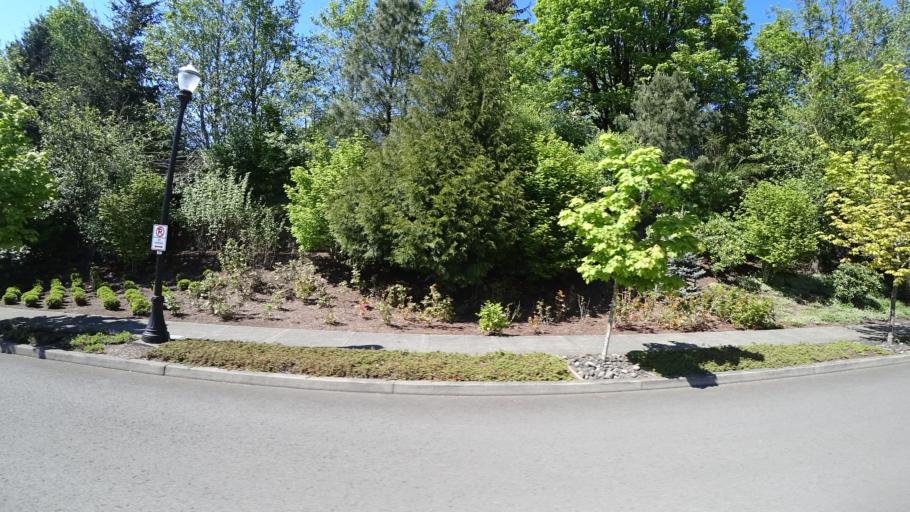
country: US
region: Oregon
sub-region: Washington County
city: West Haven
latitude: 45.5520
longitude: -122.7760
